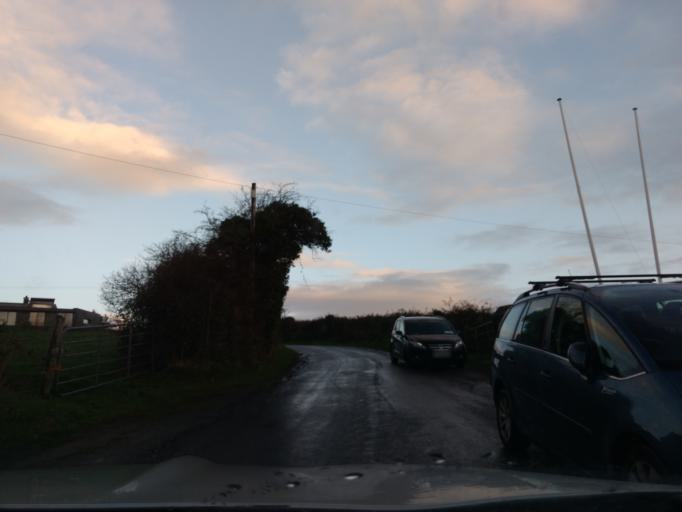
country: IE
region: Ulster
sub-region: County Donegal
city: Buncrana
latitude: 55.0954
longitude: -7.5420
